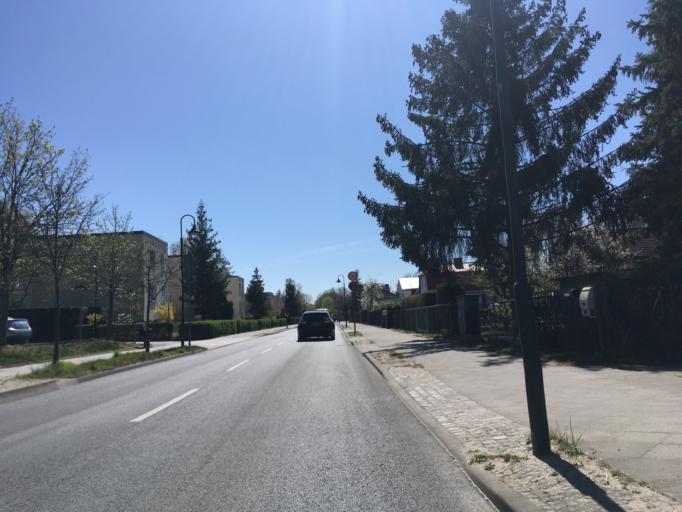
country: DE
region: Brandenburg
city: Bernau bei Berlin
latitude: 52.6699
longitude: 13.5575
